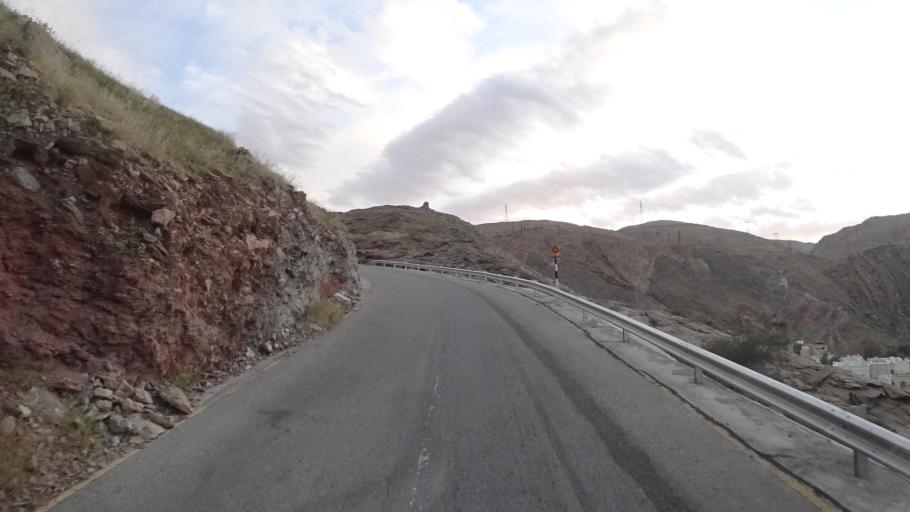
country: OM
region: Muhafazat Masqat
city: Muscat
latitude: 23.5757
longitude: 58.5500
